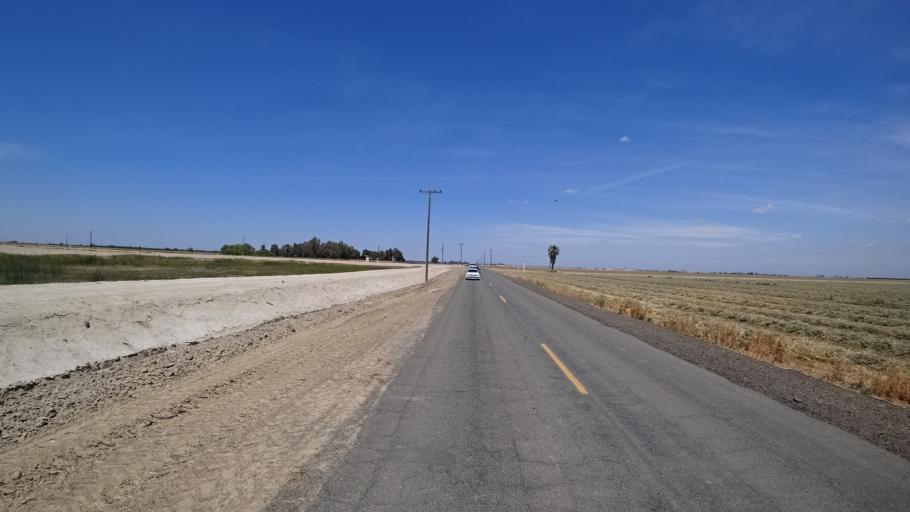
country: US
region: California
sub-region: Kings County
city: Home Garden
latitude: 36.2317
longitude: -119.6729
